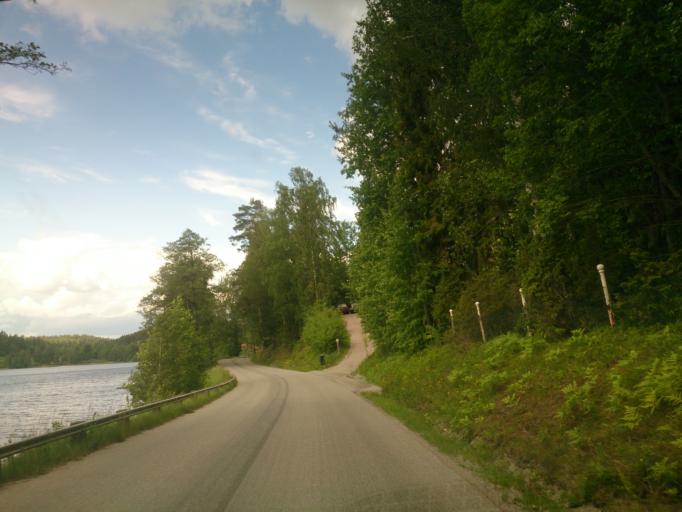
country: SE
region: OEstergoetland
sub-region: Norrkopings Kommun
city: Jursla
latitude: 58.7136
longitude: 16.1544
